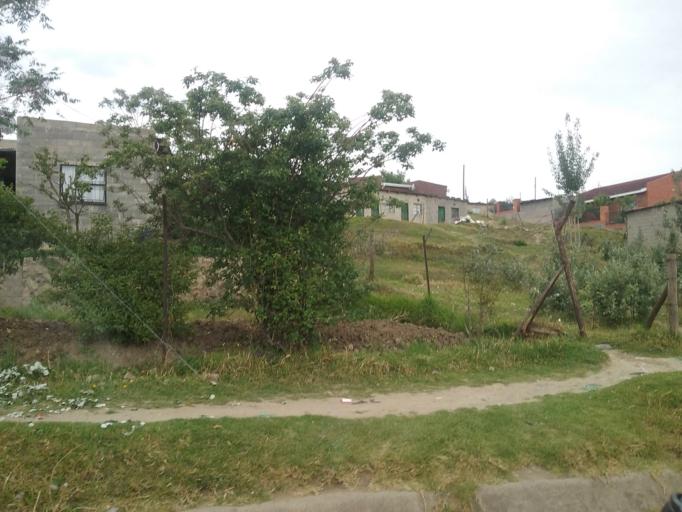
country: LS
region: Maseru
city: Maseru
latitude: -29.3251
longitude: 27.5083
